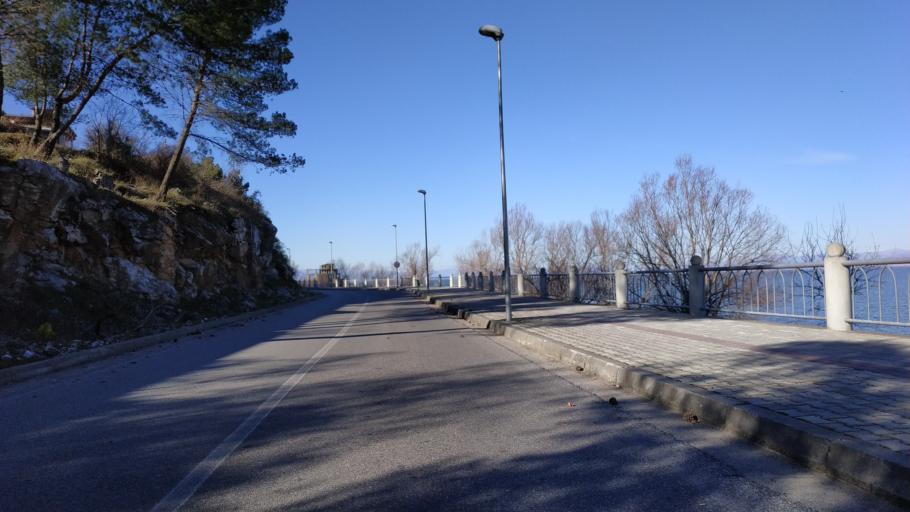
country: AL
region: Shkoder
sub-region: Rrethi i Shkodres
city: Berdica e Madhe
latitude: 42.0570
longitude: 19.4666
